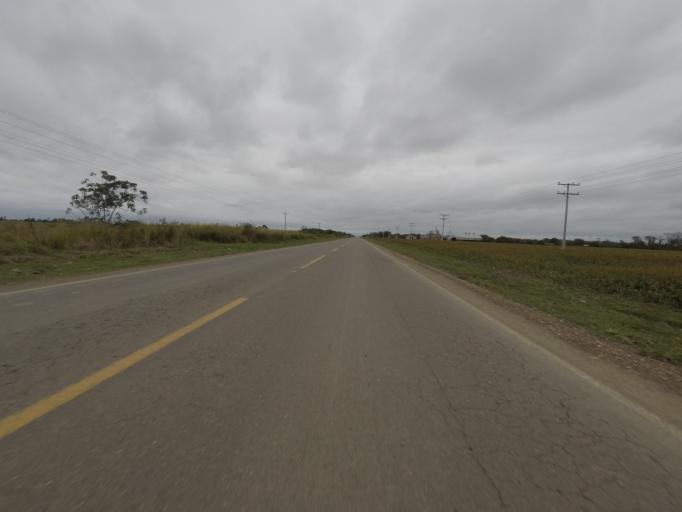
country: BO
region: Santa Cruz
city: Okinawa Numero Uno
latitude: -17.2418
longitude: -62.5554
